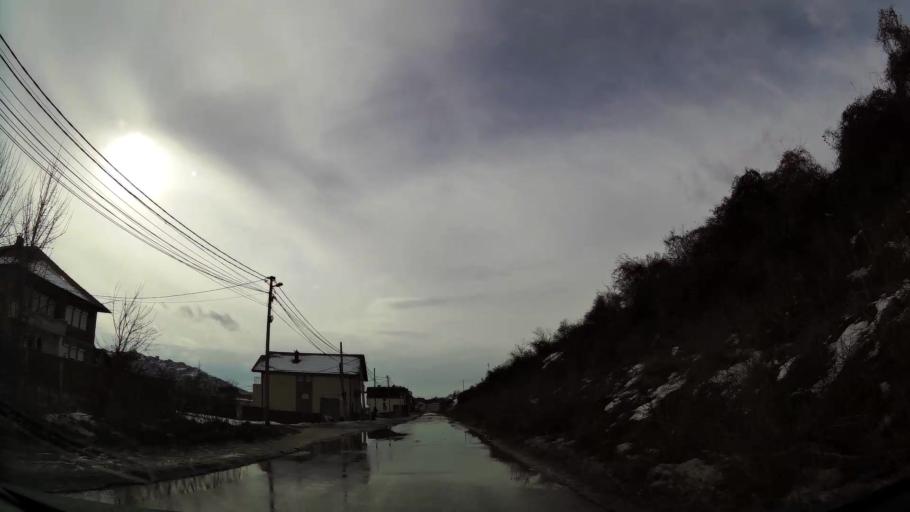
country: XK
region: Pristina
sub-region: Komuna e Prishtines
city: Pristina
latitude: 42.6878
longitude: 21.1775
